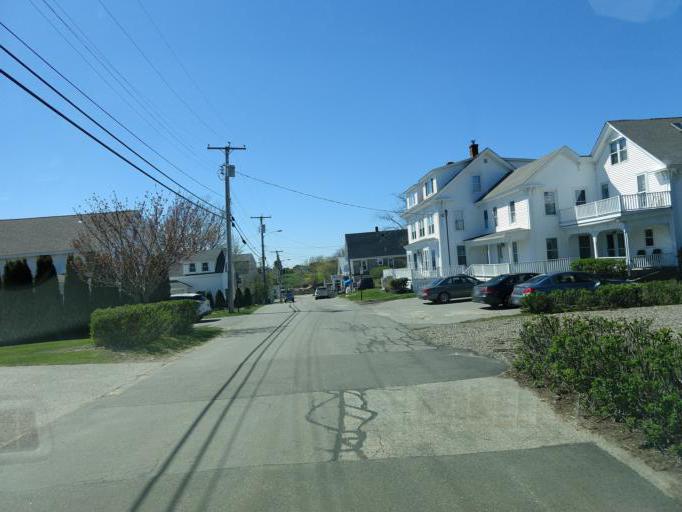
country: US
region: Maine
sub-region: York County
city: Old Orchard Beach
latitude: 43.4465
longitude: -70.3534
